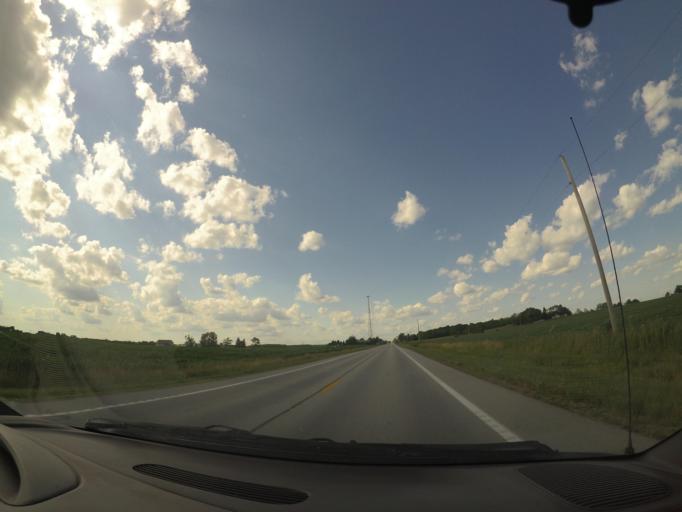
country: US
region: Ohio
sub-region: Wood County
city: Pemberville
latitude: 41.3816
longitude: -83.4164
